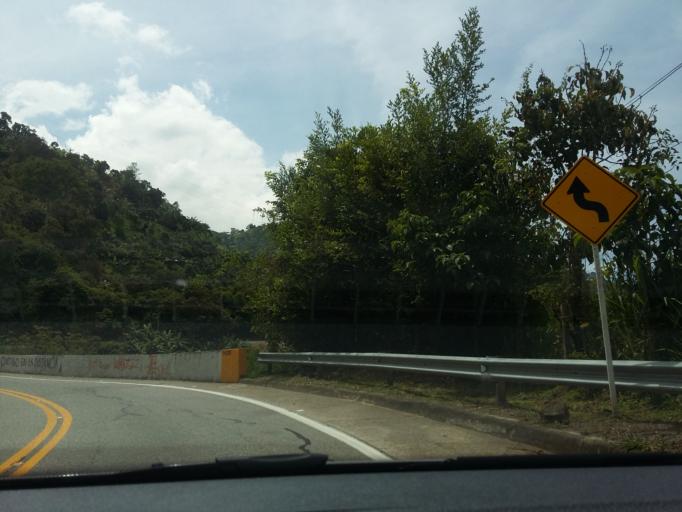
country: CO
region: Santander
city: Bucaramanga
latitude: 7.1253
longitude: -73.0907
